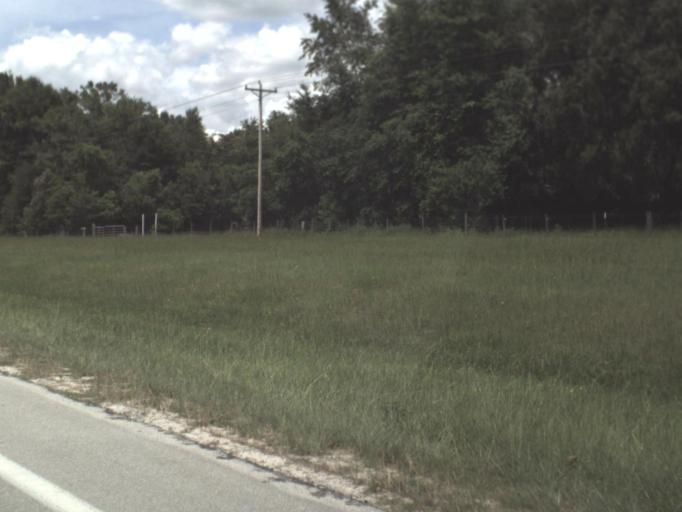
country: US
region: Florida
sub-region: Alachua County
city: High Springs
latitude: 29.7748
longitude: -82.6078
